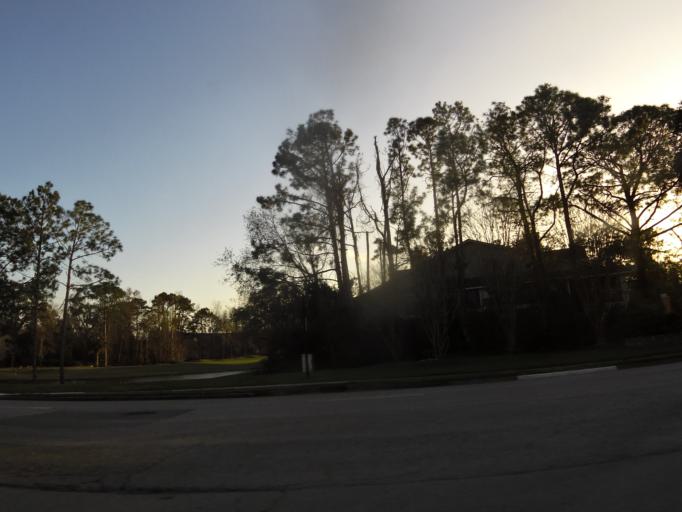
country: US
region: Florida
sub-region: Duval County
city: Jacksonville Beach
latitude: 30.2654
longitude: -81.4621
